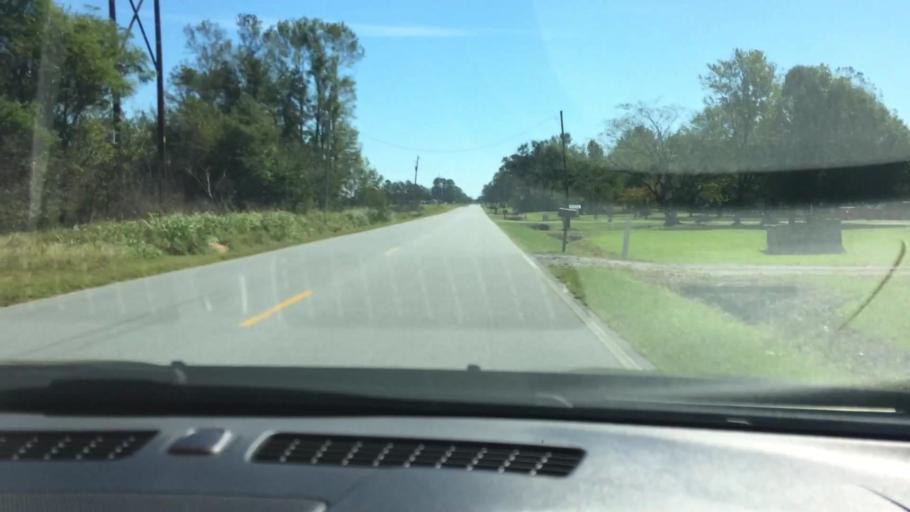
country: US
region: North Carolina
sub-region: Pitt County
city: Grifton
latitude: 35.3918
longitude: -77.3897
